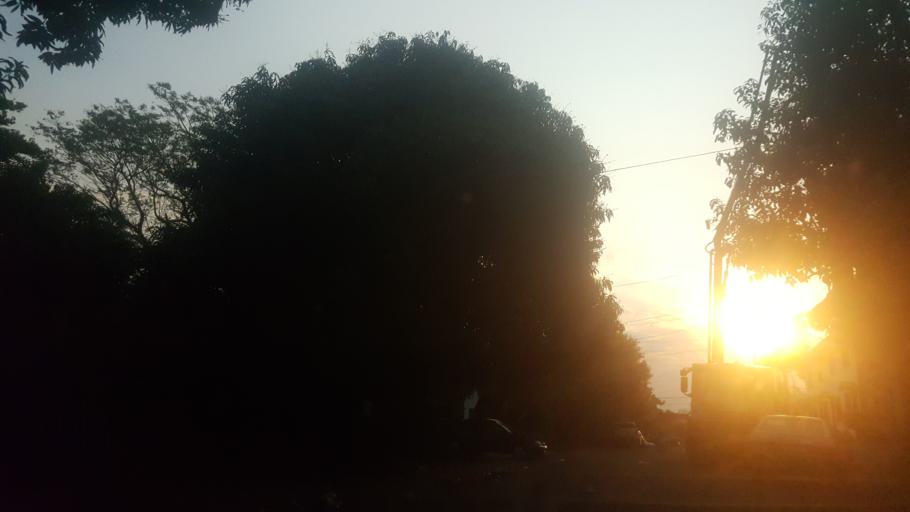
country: AR
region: Misiones
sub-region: Departamento de Capital
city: Posadas
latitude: -27.4008
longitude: -55.9126
